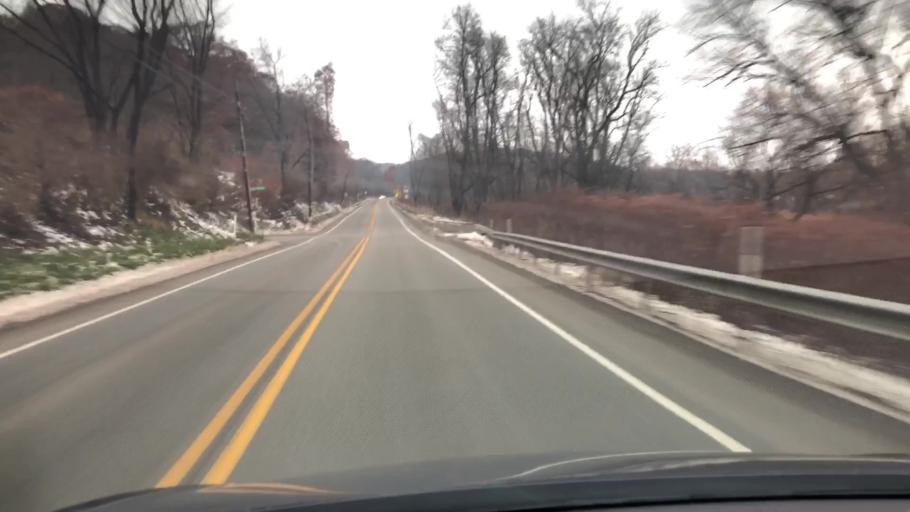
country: US
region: Pennsylvania
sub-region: Clarion County
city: Clarion
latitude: 41.0104
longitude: -79.3080
